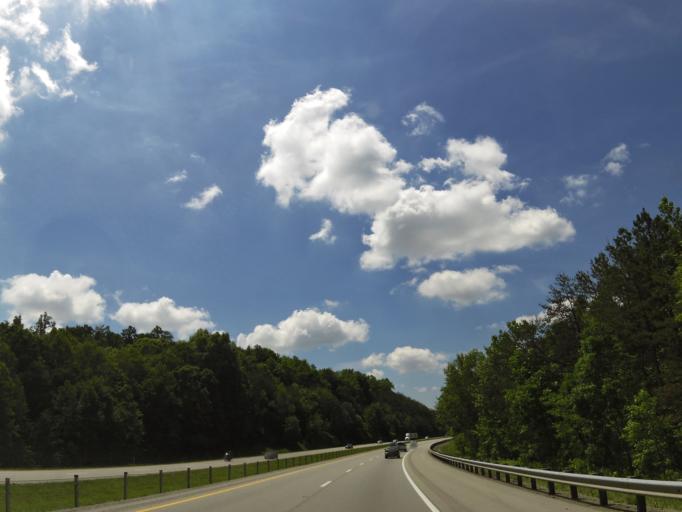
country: US
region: Kentucky
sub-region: Whitley County
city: Corbin
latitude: 36.8693
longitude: -84.1476
